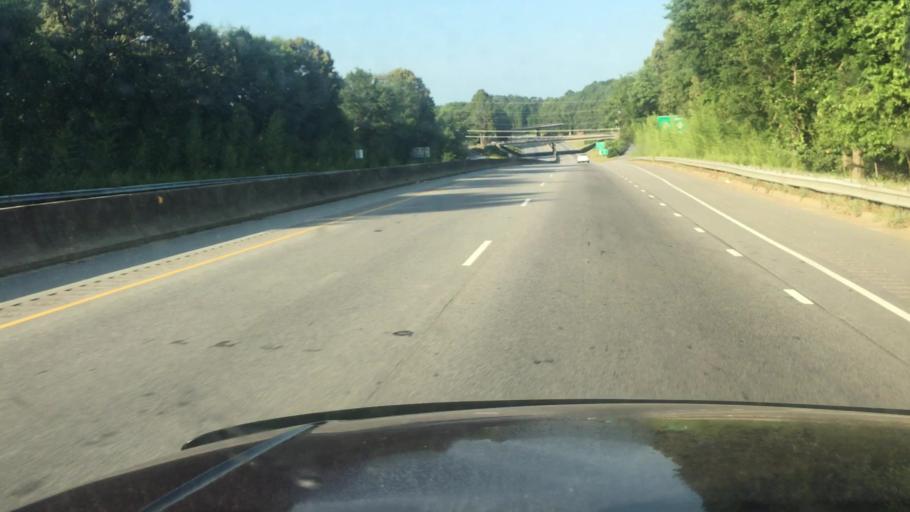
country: US
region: North Carolina
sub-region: Cumberland County
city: Fayetteville
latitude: 35.0654
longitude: -78.8878
